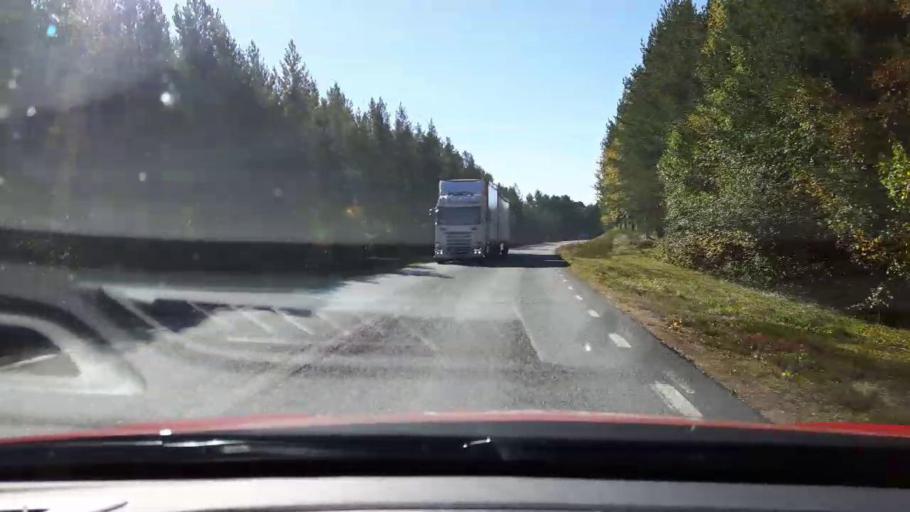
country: SE
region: Jaemtland
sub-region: Harjedalens Kommun
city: Sveg
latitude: 62.3243
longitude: 14.0619
